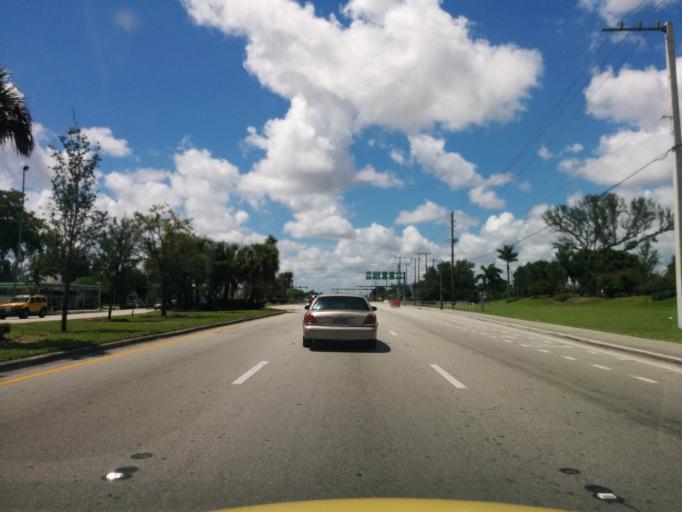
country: US
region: Florida
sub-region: Broward County
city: Davie
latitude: 26.0670
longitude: -80.2524
